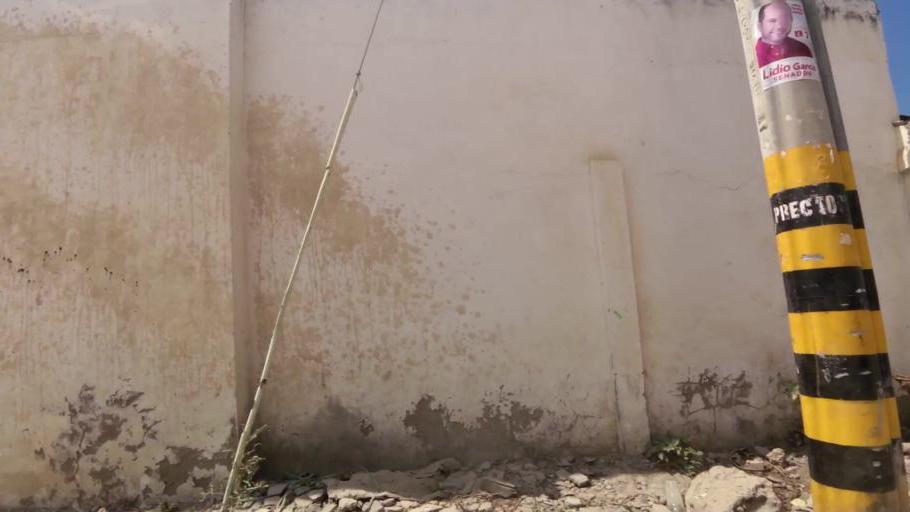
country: CO
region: Bolivar
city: Cartagena
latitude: 10.3691
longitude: -75.5081
